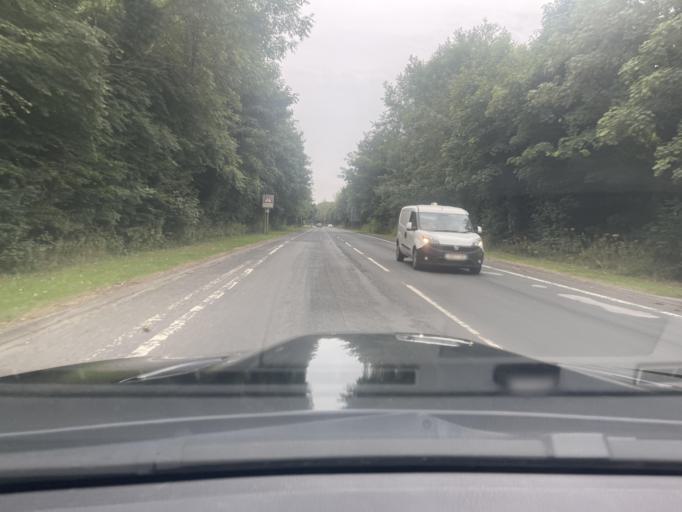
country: GB
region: England
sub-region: Lancashire
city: Leyland
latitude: 53.7003
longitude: -2.7186
